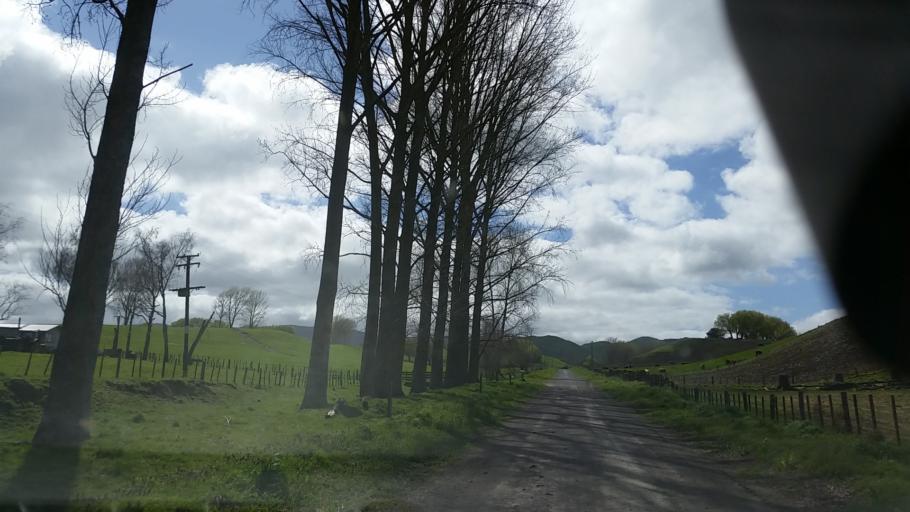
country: NZ
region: Bay of Plenty
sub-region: Rotorua District
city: Rotorua
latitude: -38.3226
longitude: 176.2964
